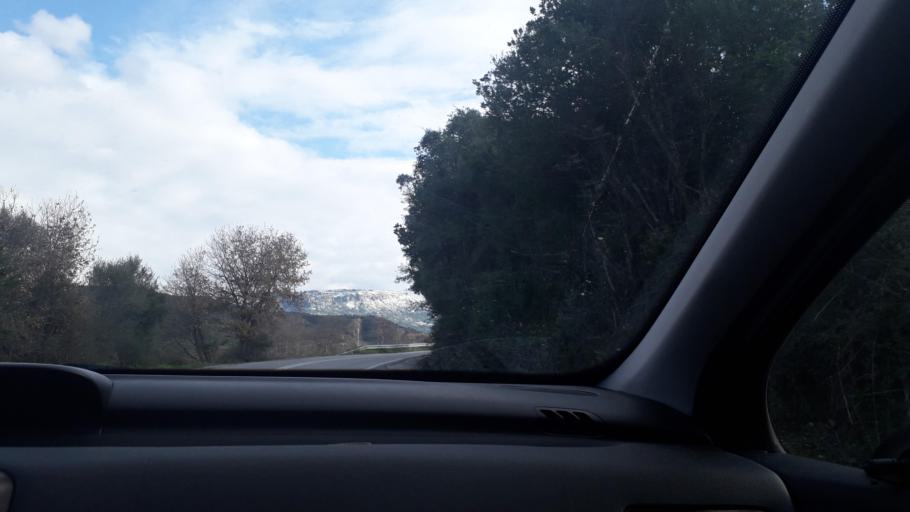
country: GR
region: Crete
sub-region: Nomos Rethymnis
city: Agia Foteini
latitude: 35.2931
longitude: 24.5582
